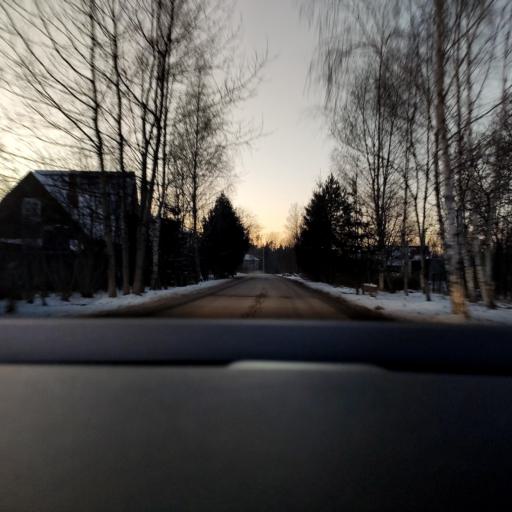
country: RU
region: Moskovskaya
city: Skhodnya
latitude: 55.8932
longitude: 37.3037
